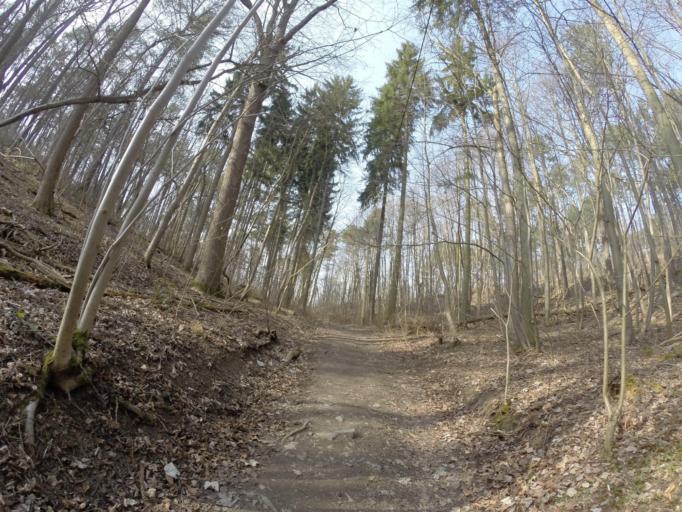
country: DE
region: Thuringia
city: Jena
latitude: 50.9409
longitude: 11.5757
